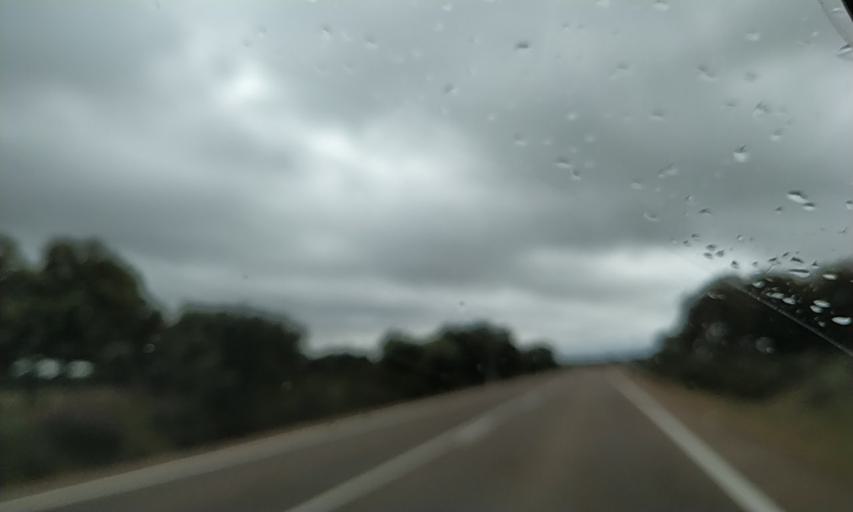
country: ES
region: Extremadura
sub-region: Provincia de Badajoz
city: Villar del Rey
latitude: 39.0366
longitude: -6.8178
